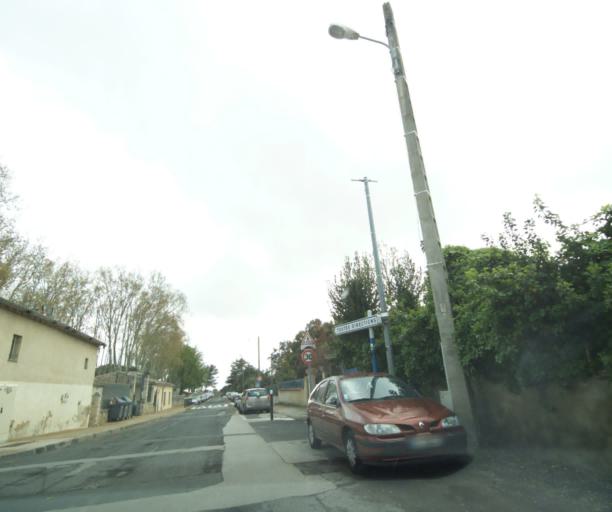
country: FR
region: Languedoc-Roussillon
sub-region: Departement de l'Herault
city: Pignan
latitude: 43.5823
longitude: 3.7605
